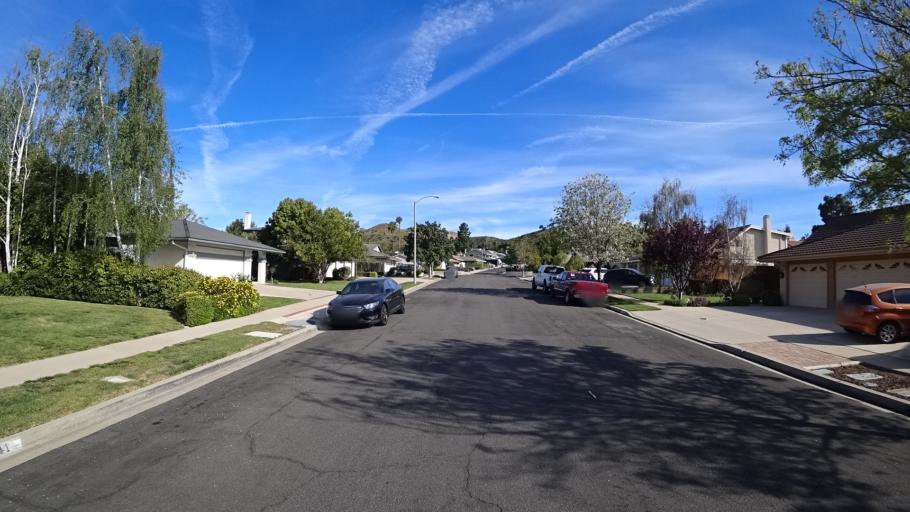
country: US
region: California
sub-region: Ventura County
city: Casa Conejo
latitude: 34.1701
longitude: -118.9628
